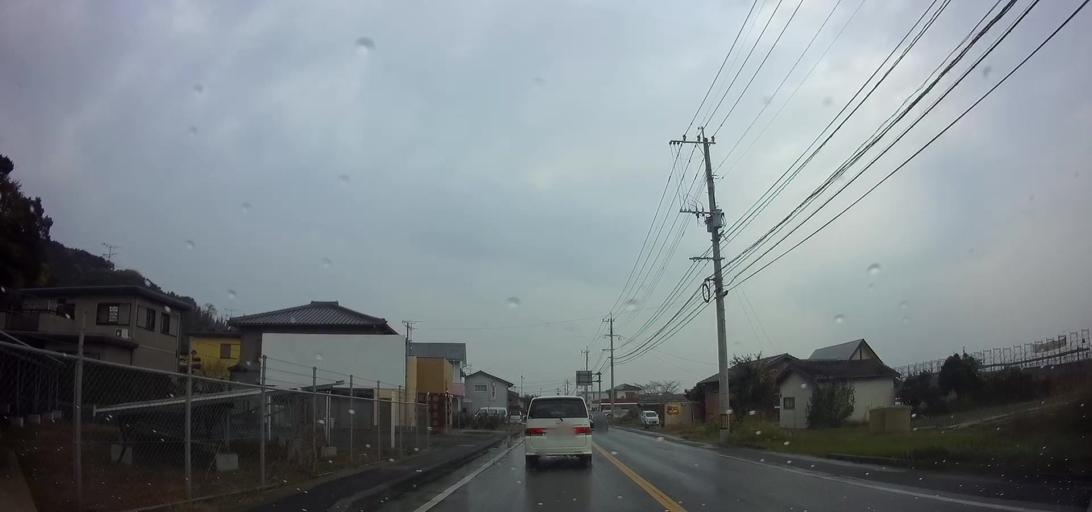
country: JP
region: Nagasaki
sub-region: Isahaya-shi
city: Isahaya
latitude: 32.8323
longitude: 130.1371
